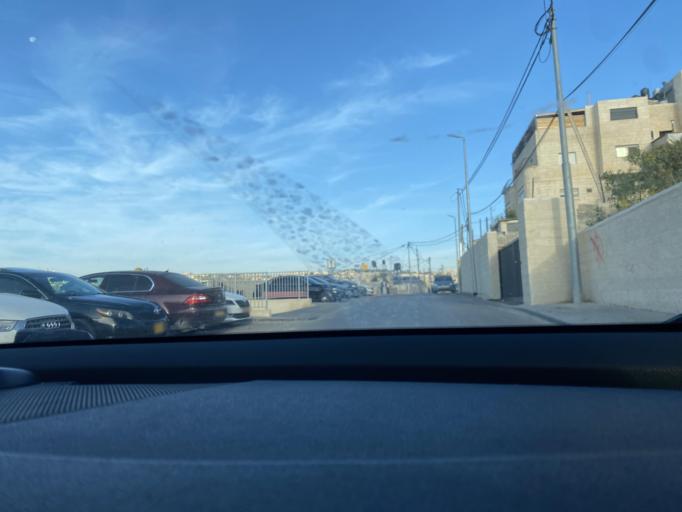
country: PS
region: West Bank
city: Ash Shaykh Sa`d
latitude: 31.7386
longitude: 35.2431
